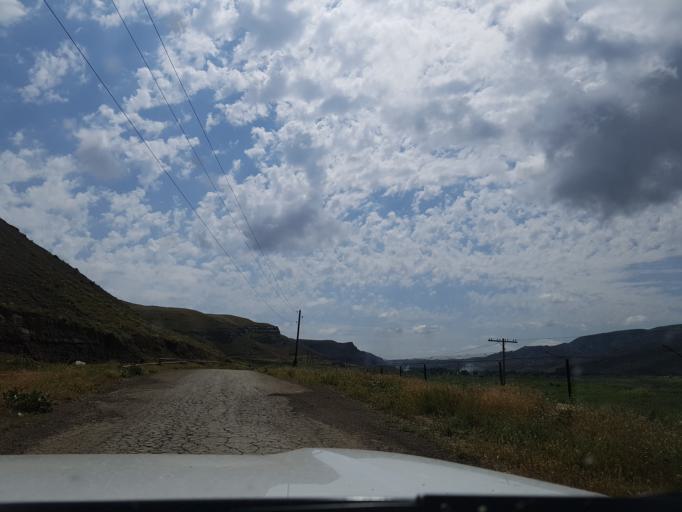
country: TM
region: Ahal
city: Baharly
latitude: 38.2298
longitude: 56.8653
